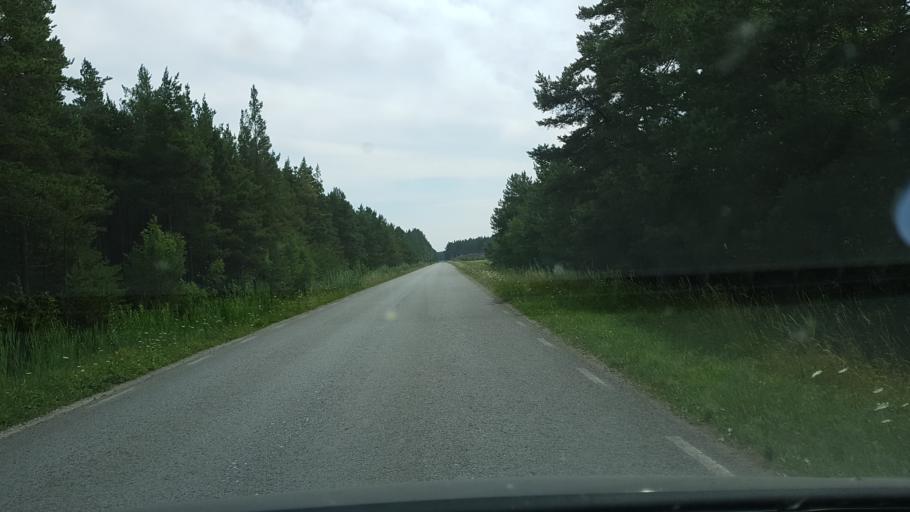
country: SE
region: Gotland
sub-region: Gotland
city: Visby
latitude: 57.7289
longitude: 18.5062
